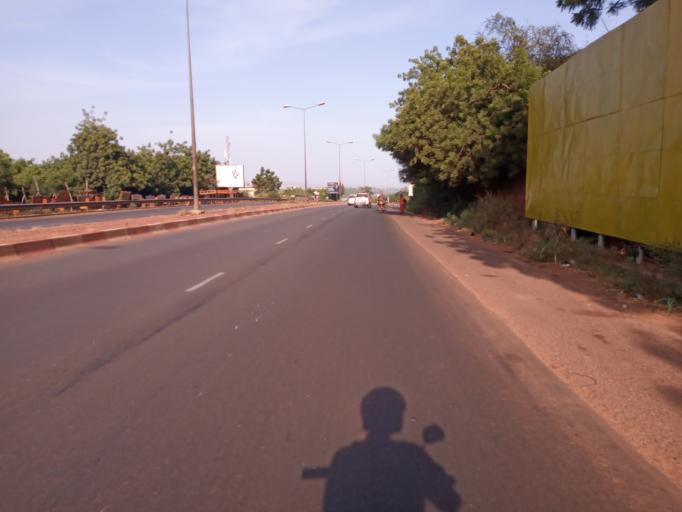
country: ML
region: Bamako
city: Bamako
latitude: 12.6178
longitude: -7.9857
